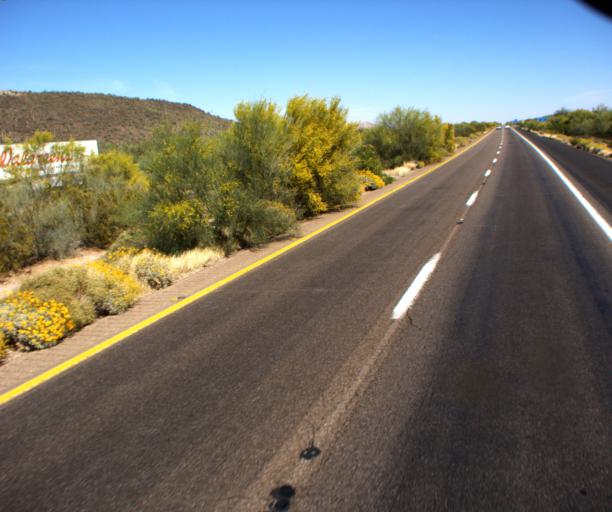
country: US
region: Arizona
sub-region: Pinal County
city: Maricopa
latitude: 32.8353
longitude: -112.1861
